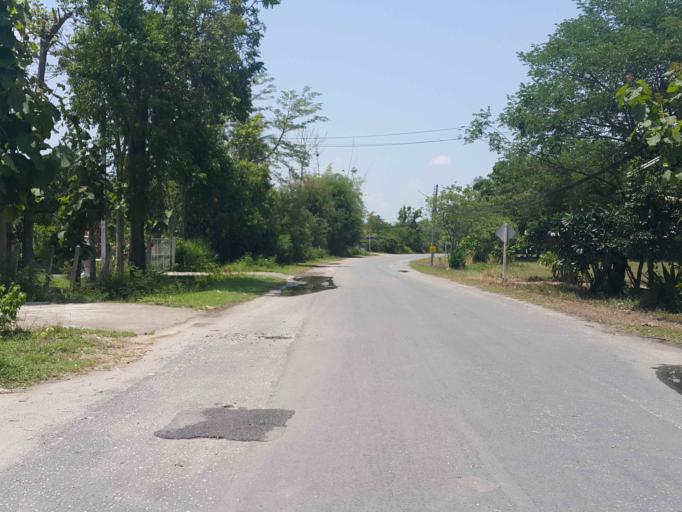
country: TH
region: Chiang Mai
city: San Sai
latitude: 18.8111
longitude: 99.0790
